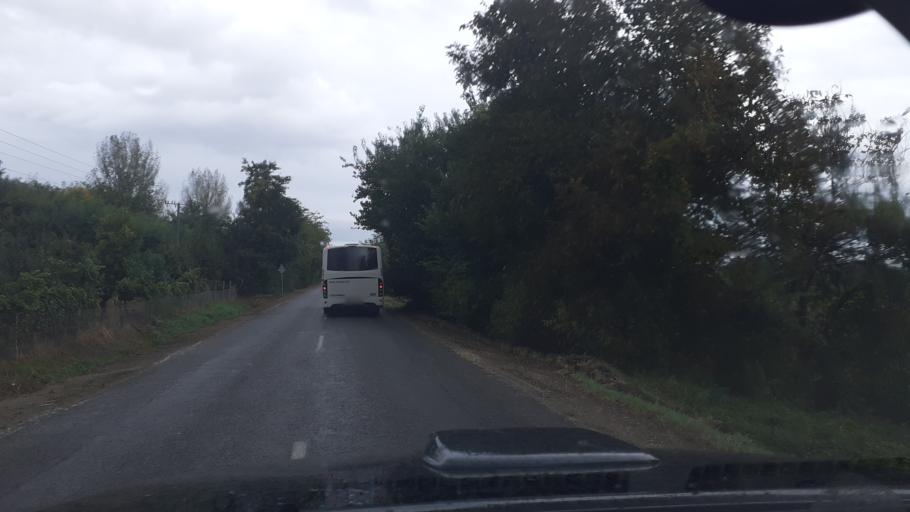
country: HU
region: Tolna
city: Bolcske
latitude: 46.7683
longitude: 18.9547
